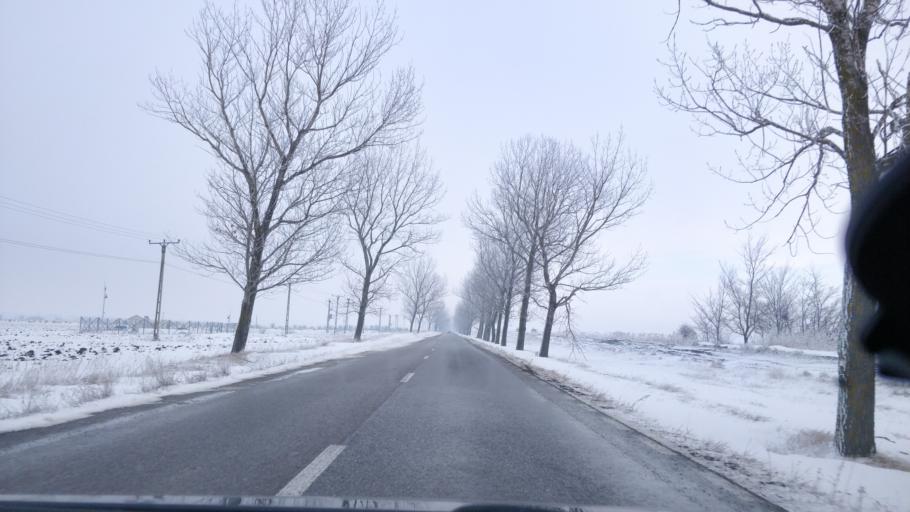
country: RO
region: Vrancea
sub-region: Comuna Vanatori
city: Jorasti
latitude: 45.6976
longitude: 27.2450
